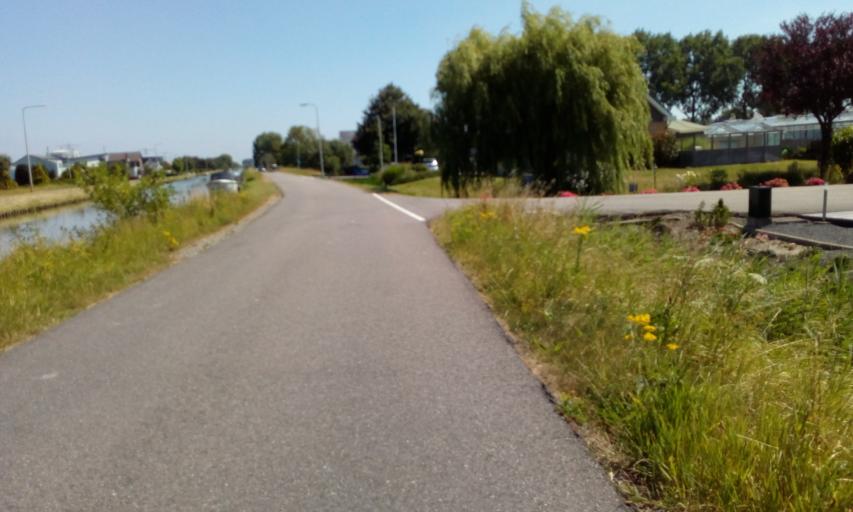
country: NL
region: South Holland
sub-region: Gemeente Westland
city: De Lier
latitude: 51.9808
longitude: 4.2316
